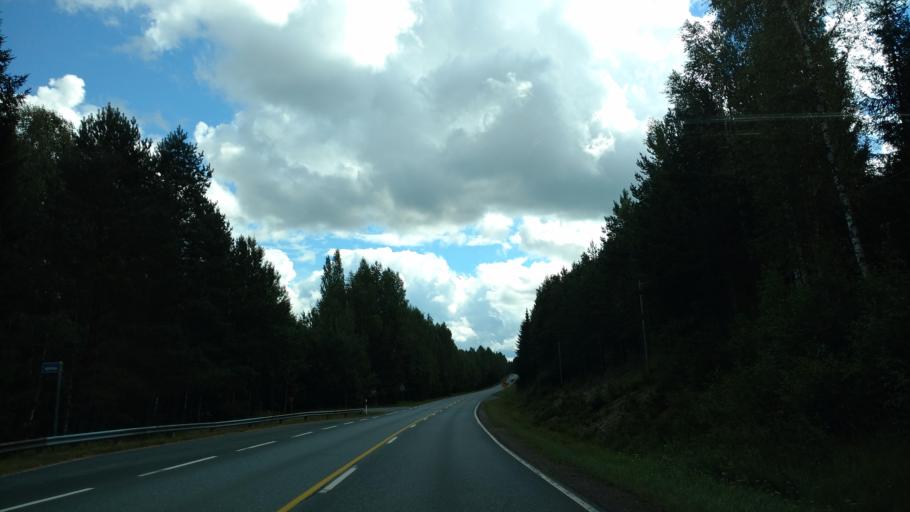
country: FI
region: Uusimaa
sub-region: Helsinki
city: Karjalohja
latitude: 60.2292
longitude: 23.6141
